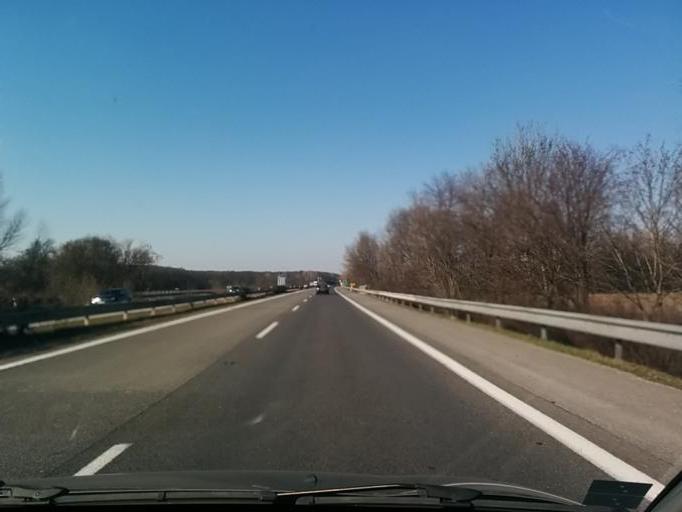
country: SK
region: Trnavsky
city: Leopoldov
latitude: 48.4439
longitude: 17.7392
